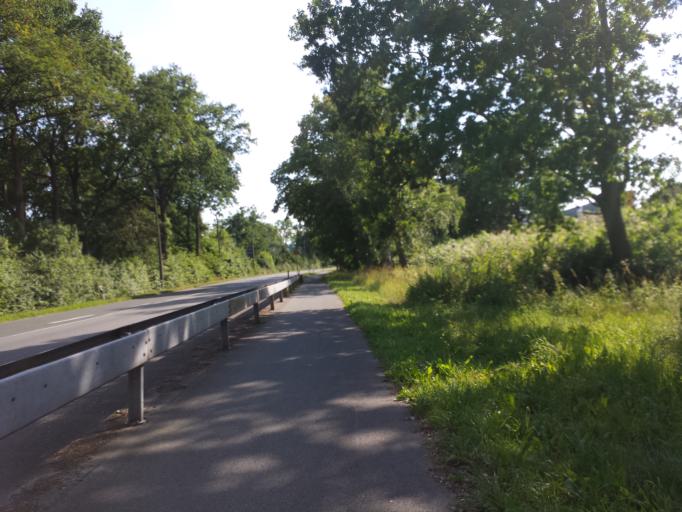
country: DE
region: Lower Saxony
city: Stuhr
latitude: 53.0835
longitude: 8.7497
